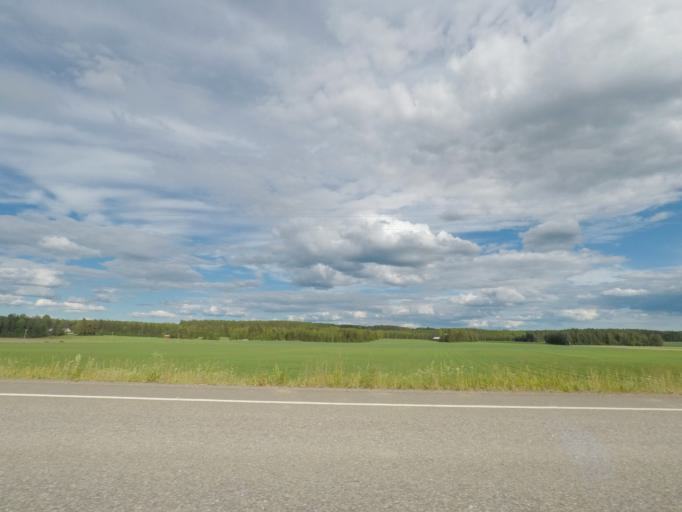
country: FI
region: Paijanne Tavastia
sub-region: Lahti
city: Hollola
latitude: 60.8551
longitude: 25.4987
